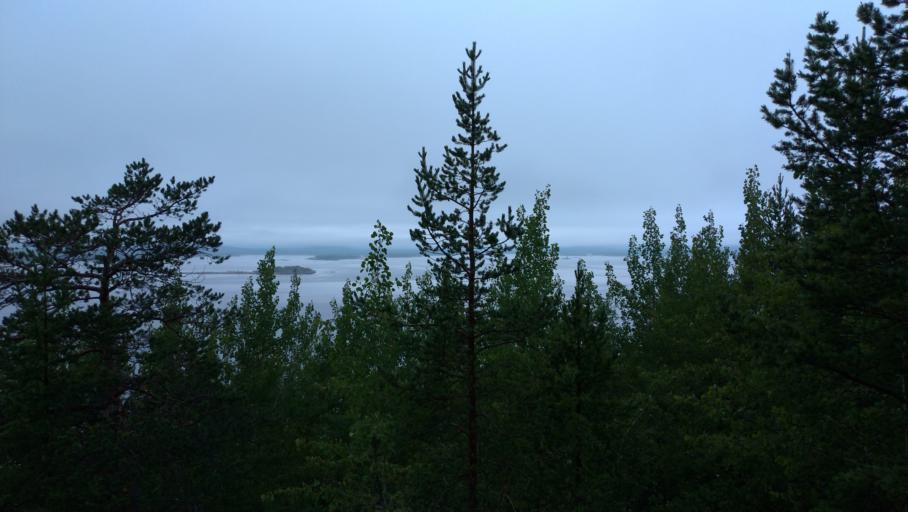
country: RU
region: Murmansk
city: Kandalaksha
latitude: 67.1238
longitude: 32.4494
